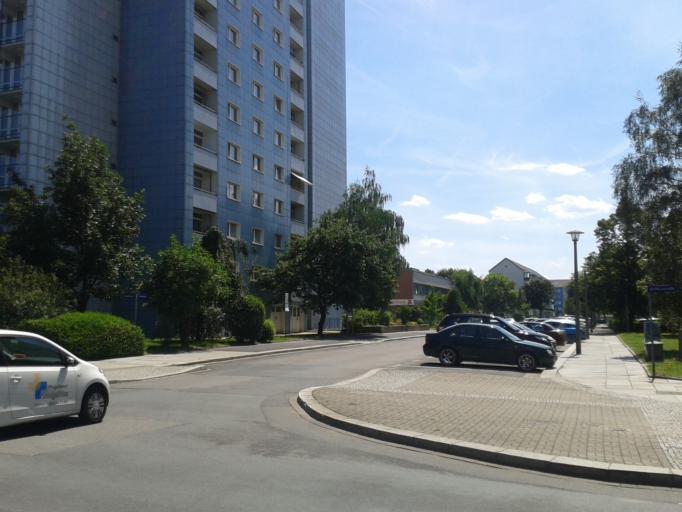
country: DE
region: Saxony
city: Dresden
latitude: 51.0496
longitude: 13.7689
